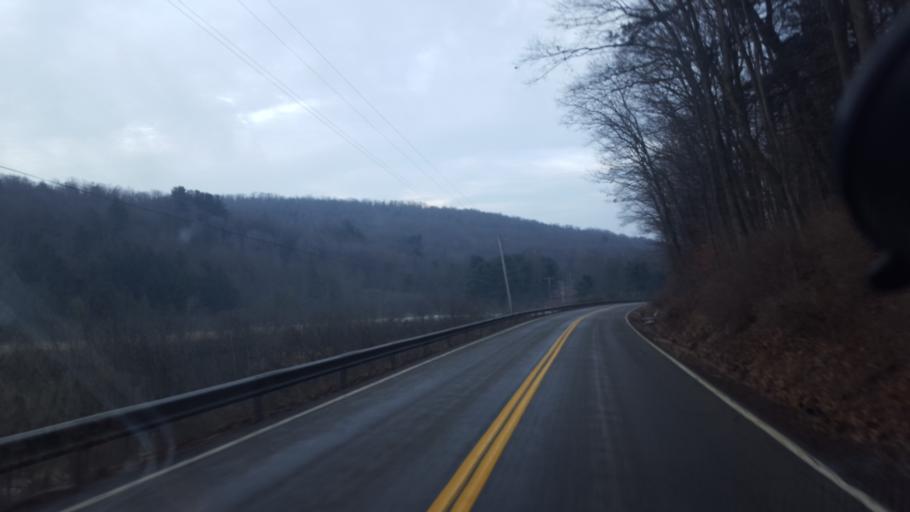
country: US
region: New York
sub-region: Allegany County
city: Andover
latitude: 42.0775
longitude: -77.7268
